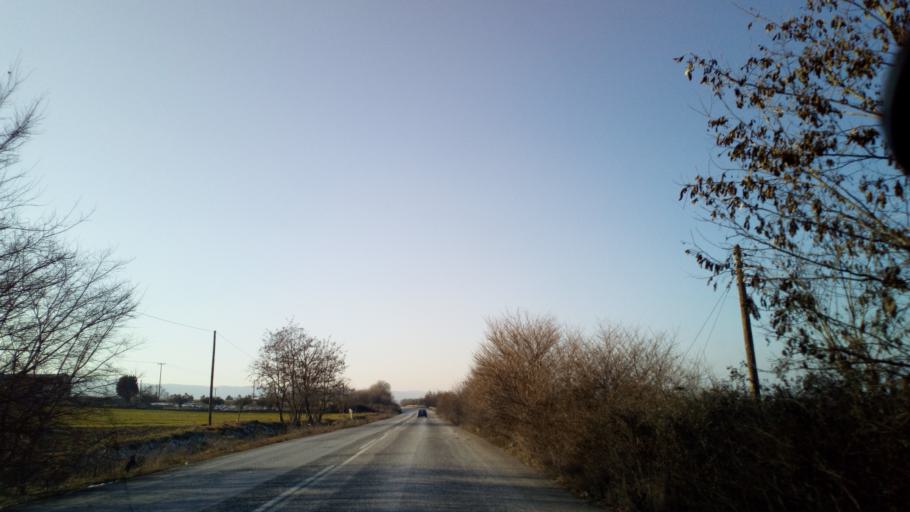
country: GR
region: Central Macedonia
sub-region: Nomos Thessalonikis
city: Agios Vasileios
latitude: 40.6552
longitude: 23.1560
